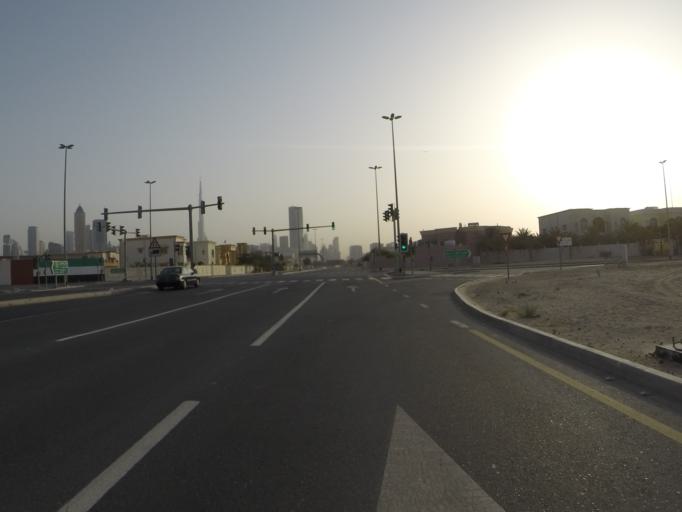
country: AE
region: Dubai
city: Dubai
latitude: 25.1660
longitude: 55.2601
